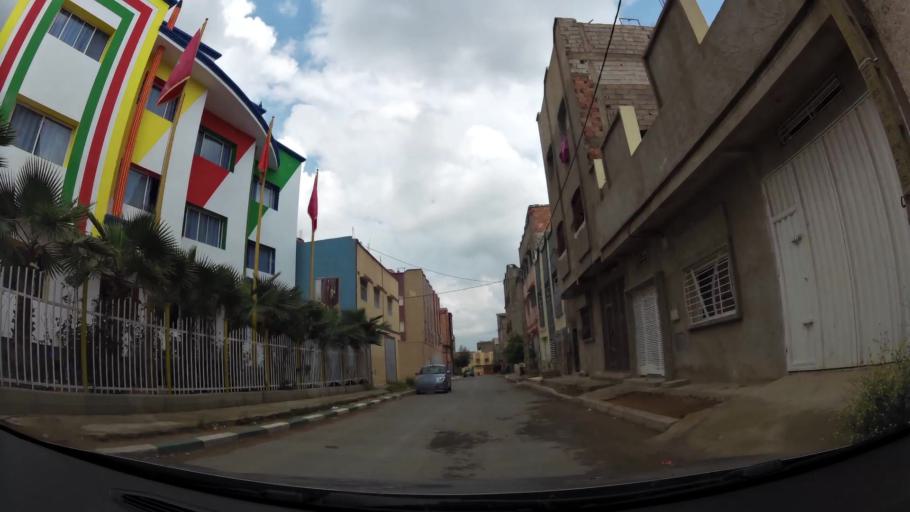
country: MA
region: Rabat-Sale-Zemmour-Zaer
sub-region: Khemisset
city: Tiflet
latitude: 33.8905
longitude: -6.3319
